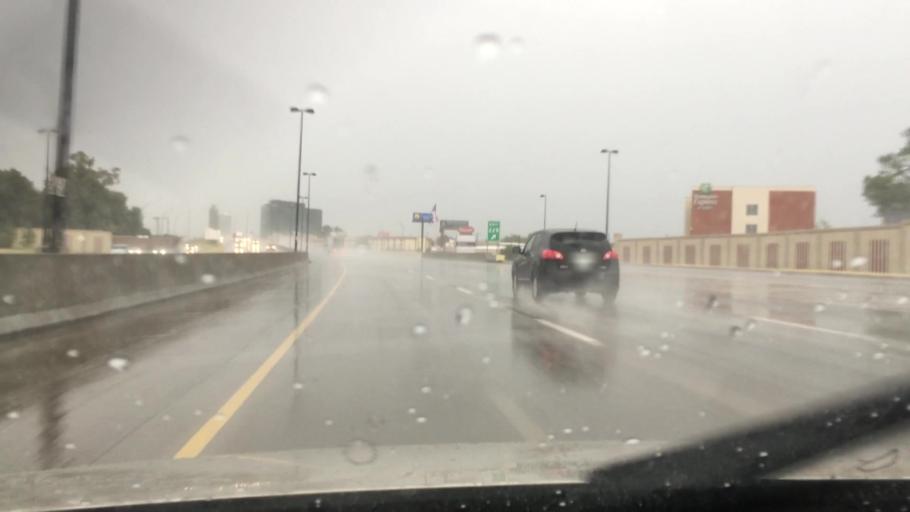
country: US
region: Oklahoma
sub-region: Tulsa County
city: Jenks
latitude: 36.0924
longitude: -95.9270
